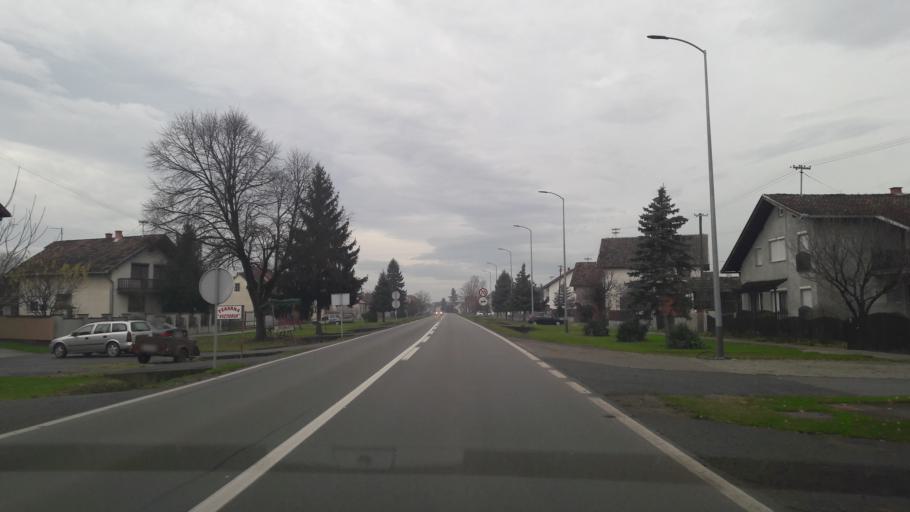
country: HR
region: Osjecko-Baranjska
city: Koska
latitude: 45.5453
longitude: 18.2829
